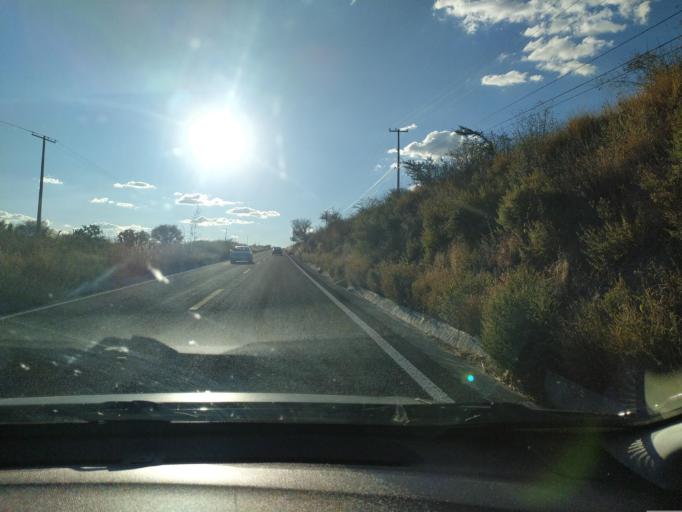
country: MX
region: Jalisco
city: San Diego de Alejandria
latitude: 21.0206
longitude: -101.9481
